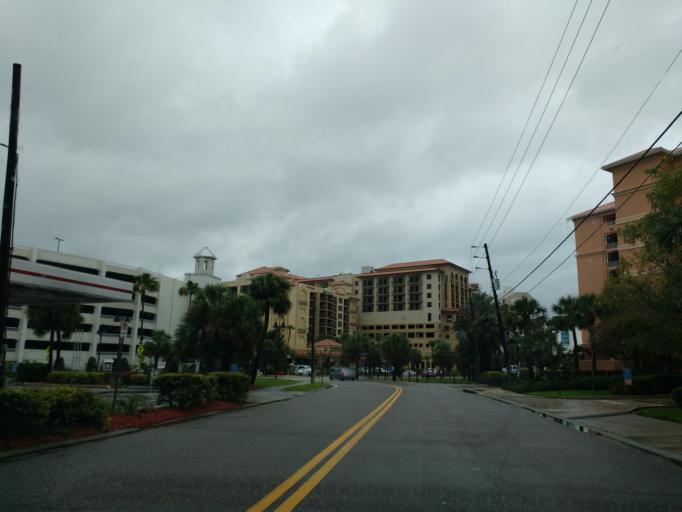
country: US
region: Florida
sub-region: Pinellas County
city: Clearwater
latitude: 27.9679
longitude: -82.8265
